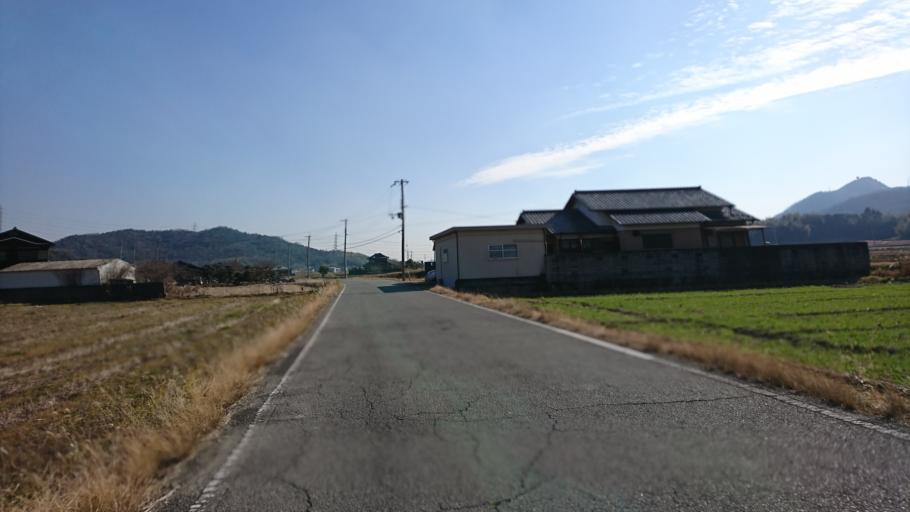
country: JP
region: Hyogo
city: Kakogawacho-honmachi
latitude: 34.8222
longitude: 134.8457
